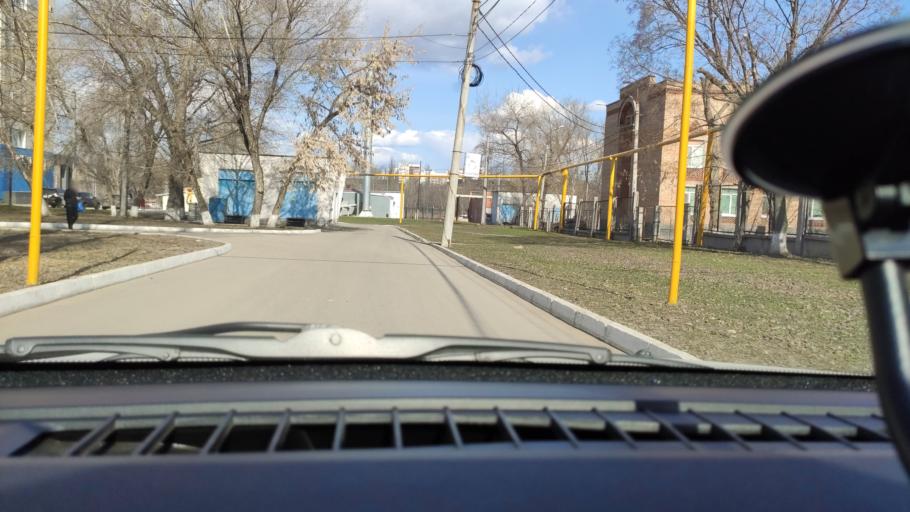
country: RU
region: Samara
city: Samara
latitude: 53.2045
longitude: 50.1683
